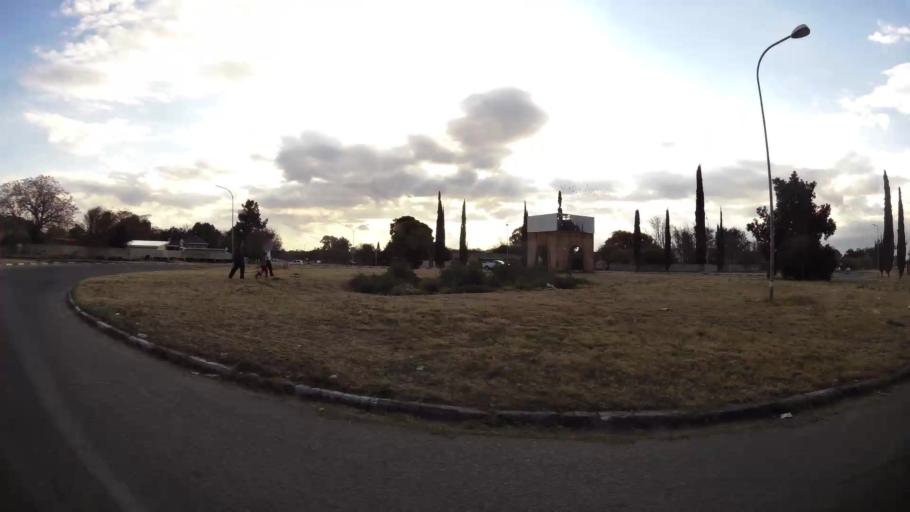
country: ZA
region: Orange Free State
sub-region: Lejweleputswa District Municipality
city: Welkom
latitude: -27.9820
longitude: 26.7120
